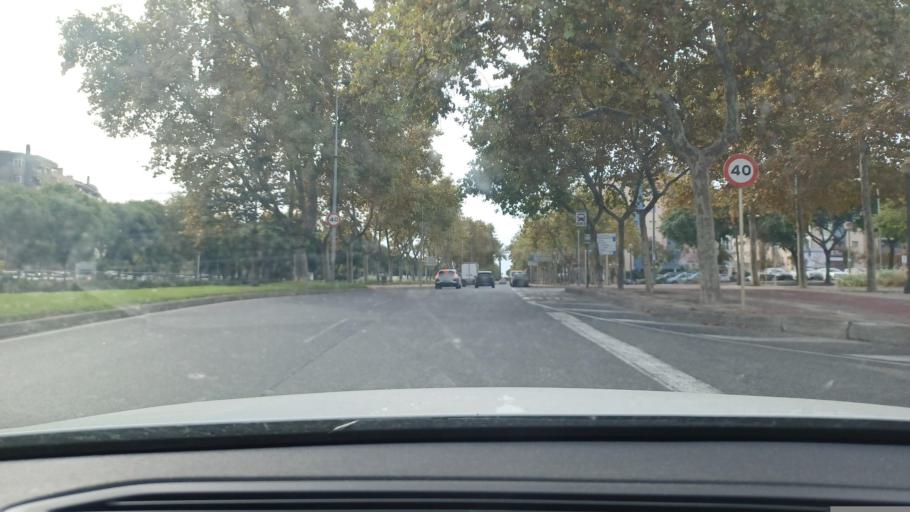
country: ES
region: Catalonia
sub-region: Provincia de Tarragona
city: Cambrils
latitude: 41.0691
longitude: 1.0558
